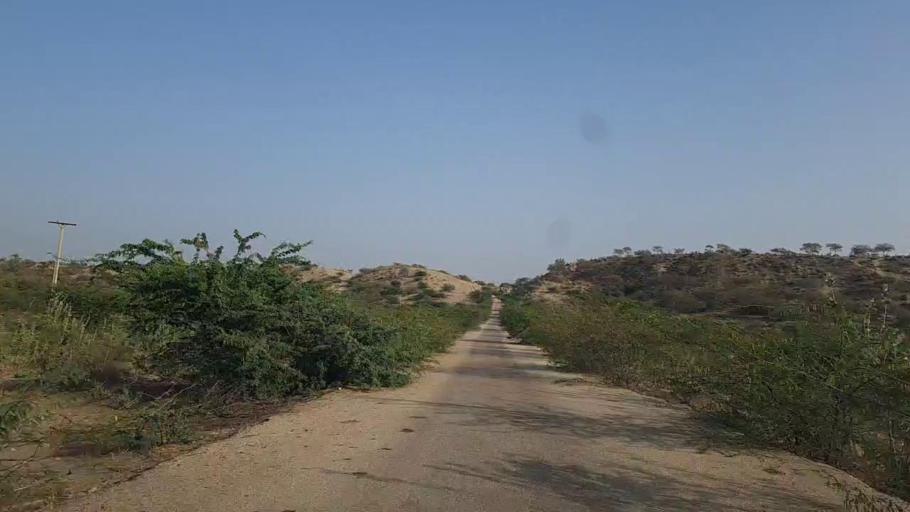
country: PK
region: Sindh
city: Diplo
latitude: 24.5988
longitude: 69.3840
